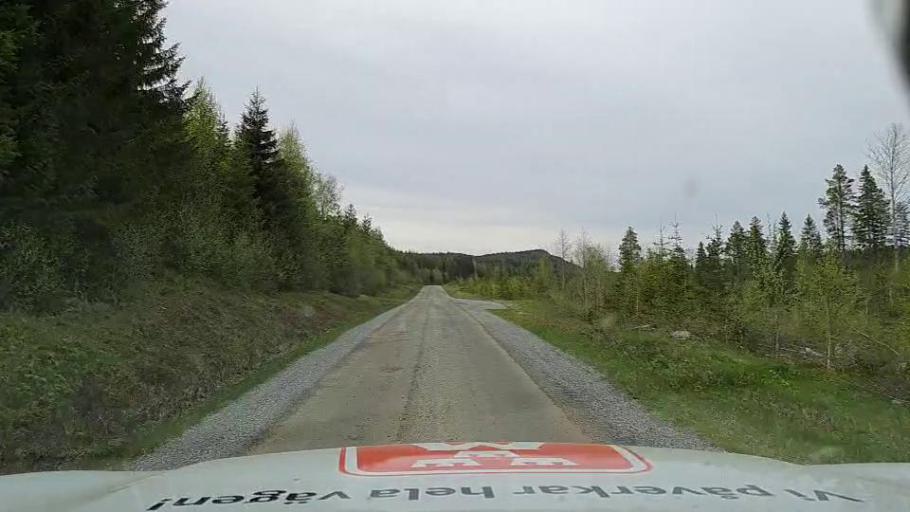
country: SE
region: Jaemtland
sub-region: Bergs Kommun
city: Hoverberg
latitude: 62.5419
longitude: 14.9028
